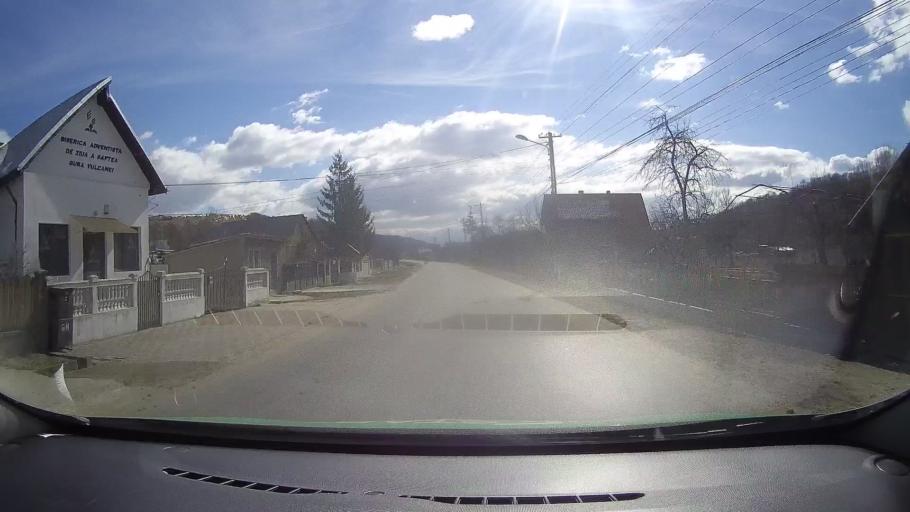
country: RO
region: Dambovita
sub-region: Comuna Vulcana-Pandele
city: Gura Vulcanei
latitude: 45.0368
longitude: 25.3912
